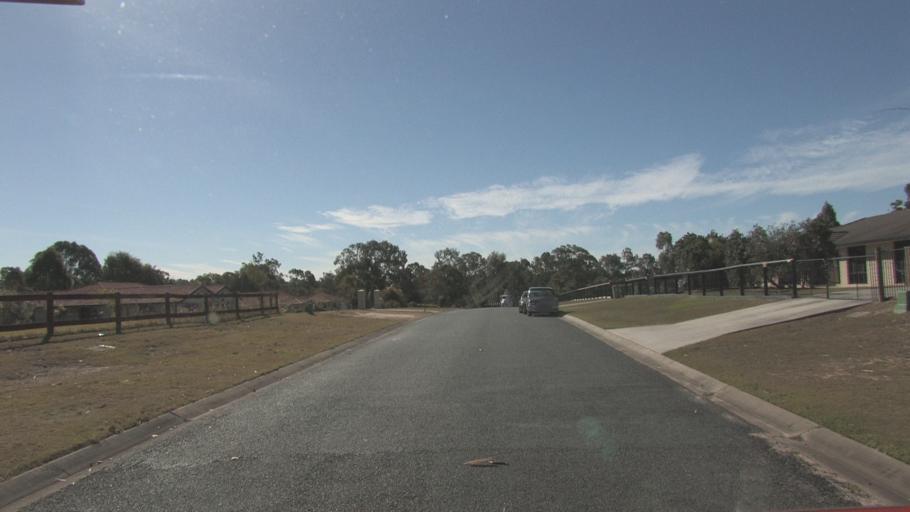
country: AU
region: Queensland
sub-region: Ipswich
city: Springfield Lakes
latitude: -27.7294
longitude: 152.9420
